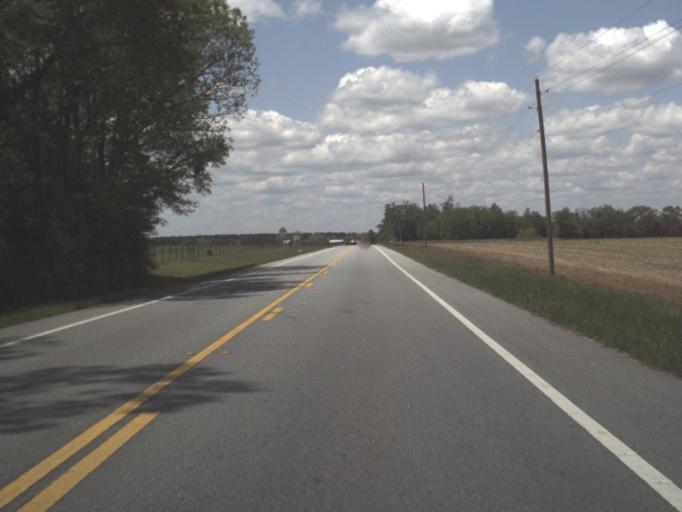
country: US
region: Florida
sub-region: Escambia County
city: Molino
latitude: 30.7444
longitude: -87.3661
